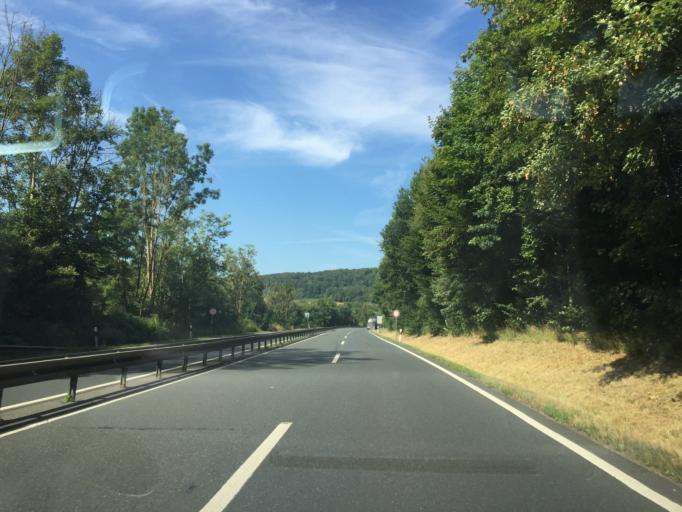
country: DE
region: Lower Saxony
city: Seesen
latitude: 51.8666
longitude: 10.1394
